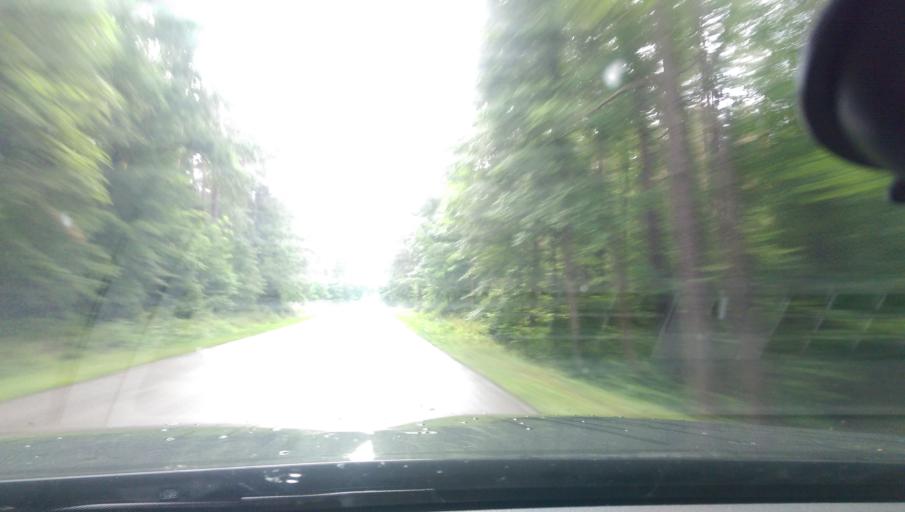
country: PL
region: Warmian-Masurian Voivodeship
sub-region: Powiat mragowski
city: Piecki
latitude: 53.7185
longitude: 21.4233
